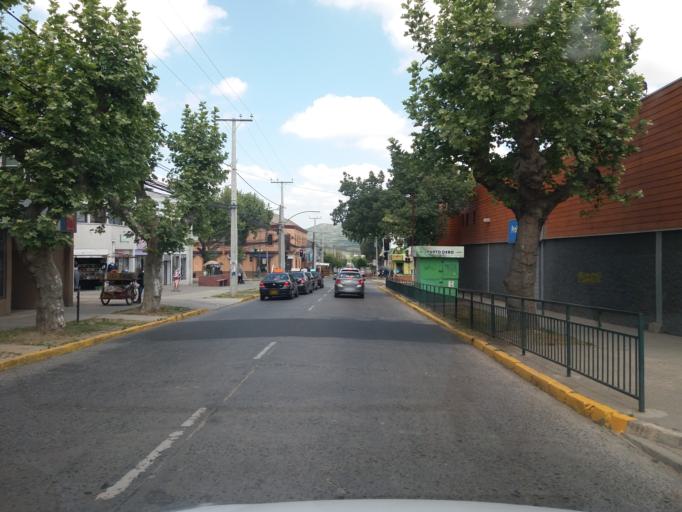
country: CL
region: Valparaiso
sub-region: Provincia de Marga Marga
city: Limache
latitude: -32.9841
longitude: -71.2767
